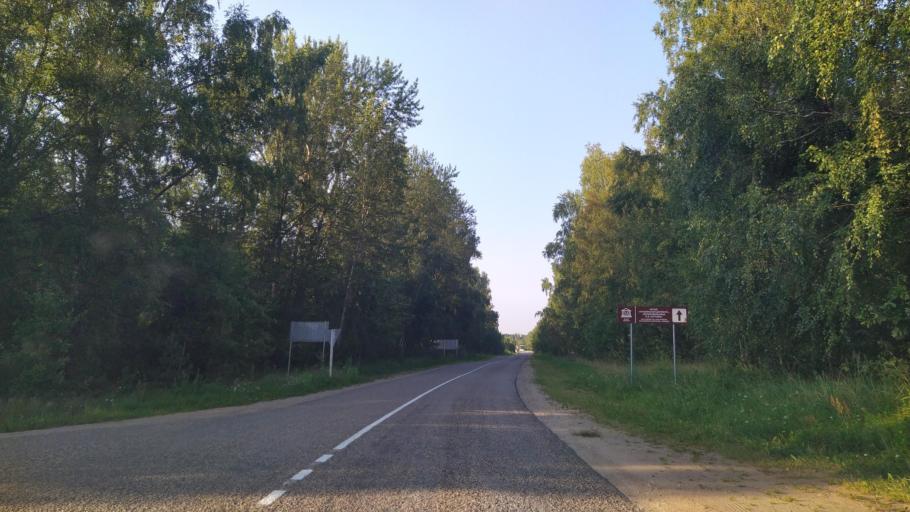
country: RU
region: Pskov
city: Pushkinskiye Gory
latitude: 57.0380
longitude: 28.9116
